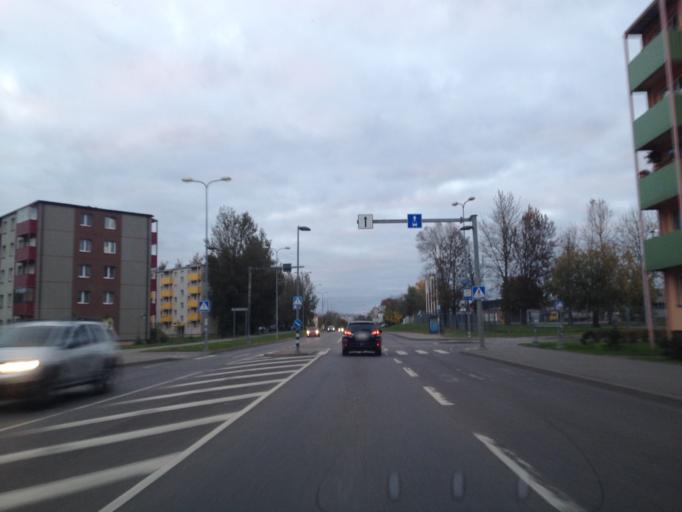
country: EE
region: Harju
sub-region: Tallinna linn
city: Tallinn
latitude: 59.4297
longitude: 24.8063
